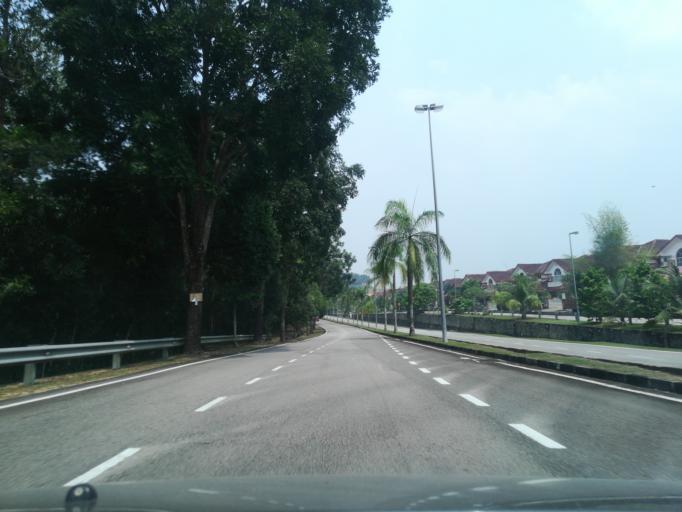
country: MY
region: Kedah
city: Kulim
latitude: 5.3959
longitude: 100.5807
